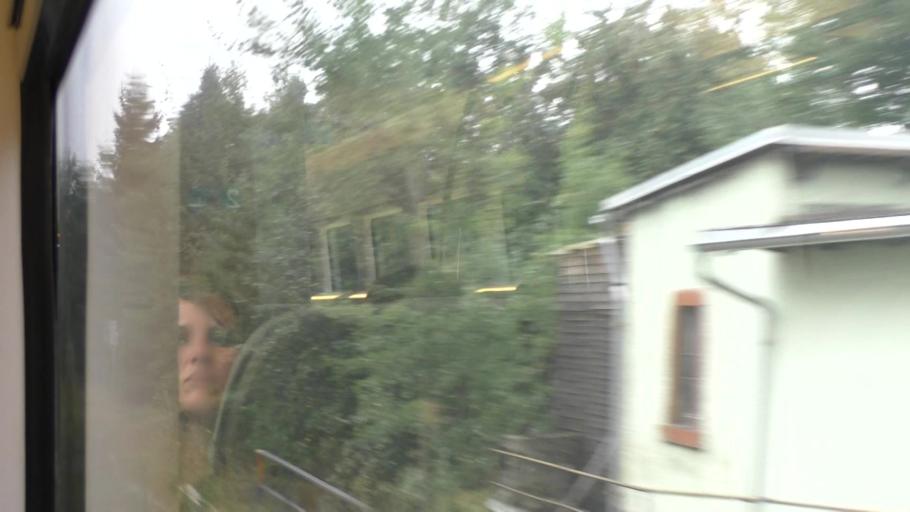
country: DE
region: Saxony
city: Ebersbach
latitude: 50.9923
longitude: 14.5850
